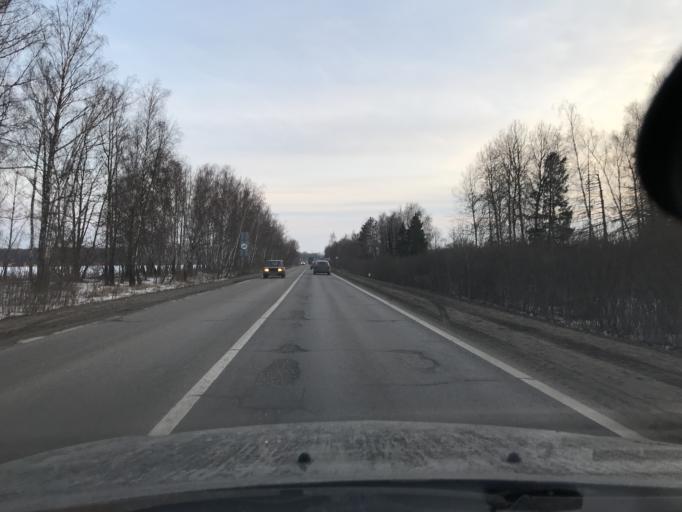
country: RU
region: Kaluga
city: Kaluga
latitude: 54.6132
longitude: 36.2760
